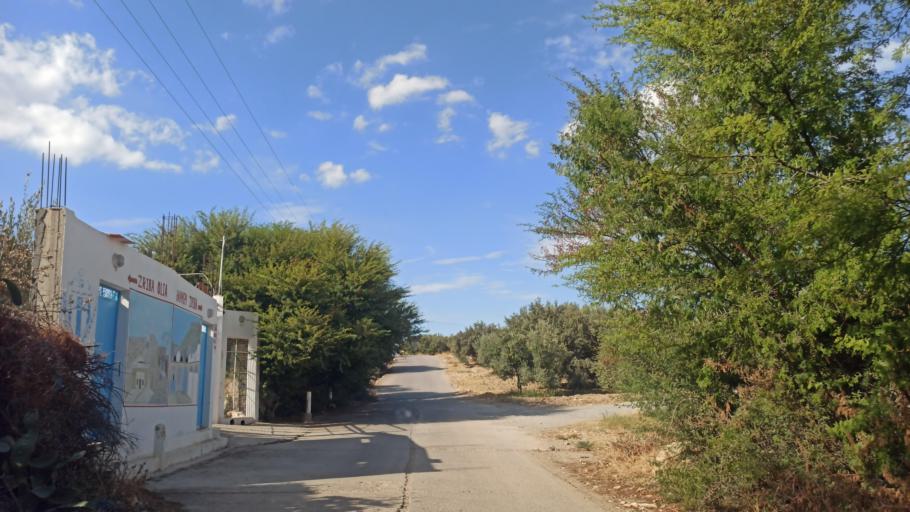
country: TN
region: Zaghwan
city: Zaghouan
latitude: 36.3339
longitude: 10.2124
